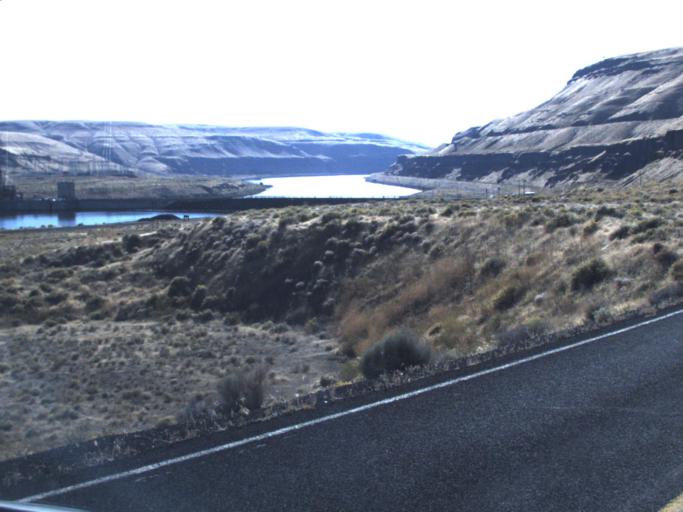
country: US
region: Washington
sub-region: Franklin County
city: Connell
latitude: 46.5694
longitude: -118.5384
